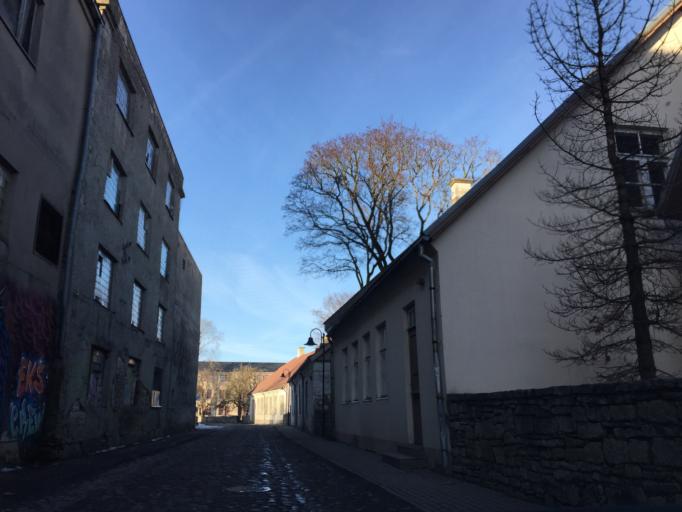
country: EE
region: Saare
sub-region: Kuressaare linn
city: Kuressaare
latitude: 58.2550
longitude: 22.4831
